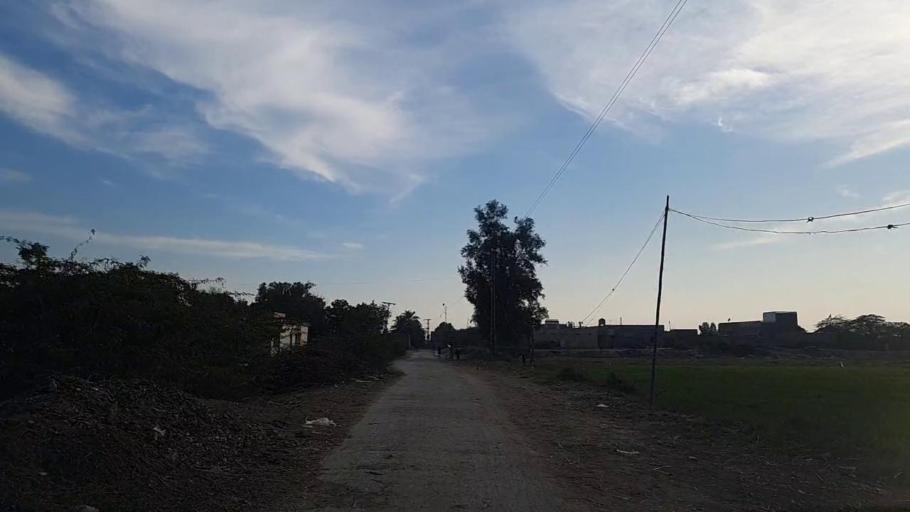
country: PK
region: Sindh
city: Bandhi
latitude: 26.5632
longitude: 68.2786
